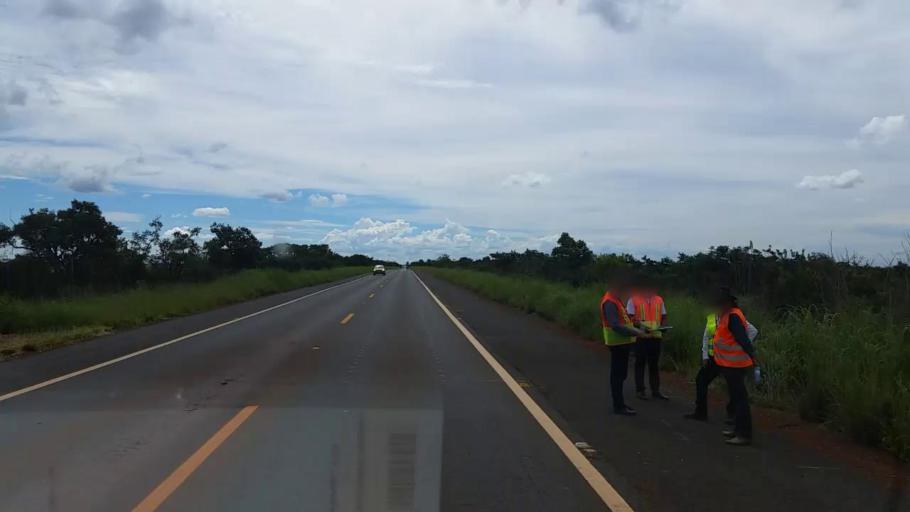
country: BR
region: Goias
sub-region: Luziania
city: Luziania
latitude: -16.2092
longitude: -47.4212
